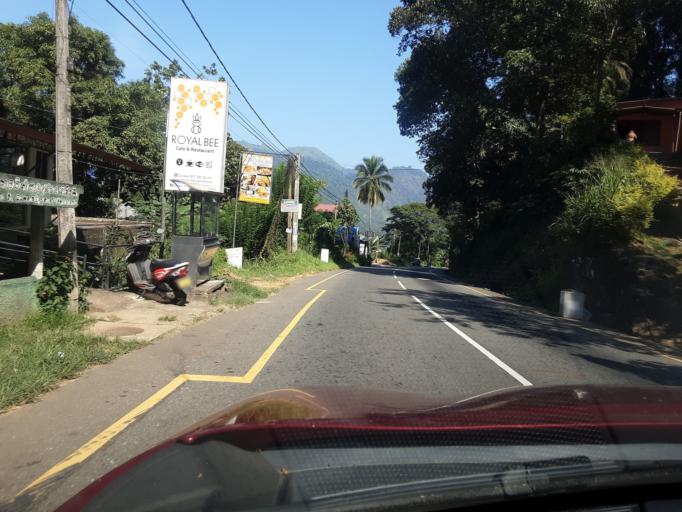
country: LK
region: Uva
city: Badulla
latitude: 7.0163
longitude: 81.0548
